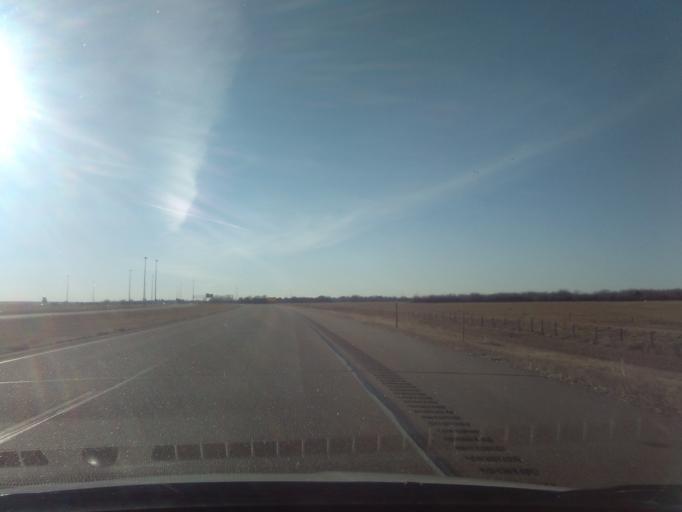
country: US
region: Colorado
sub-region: Sedgwick County
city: Julesburg
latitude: 41.0353
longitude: -102.1391
